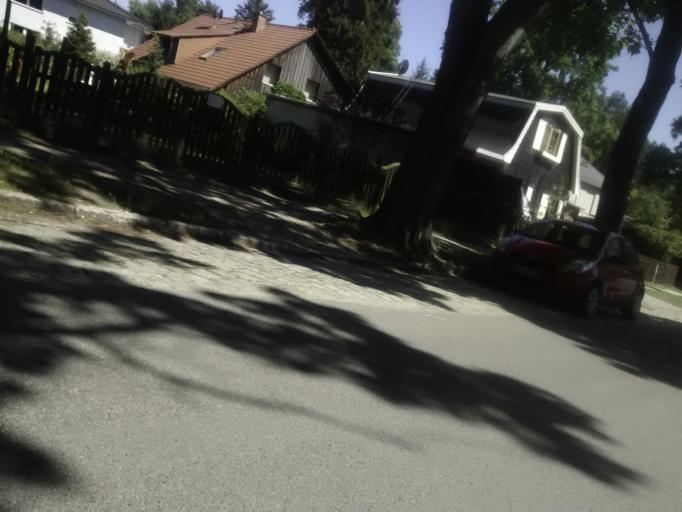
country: DE
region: Brandenburg
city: Hohen Neuendorf
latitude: 52.6811
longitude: 13.2668
